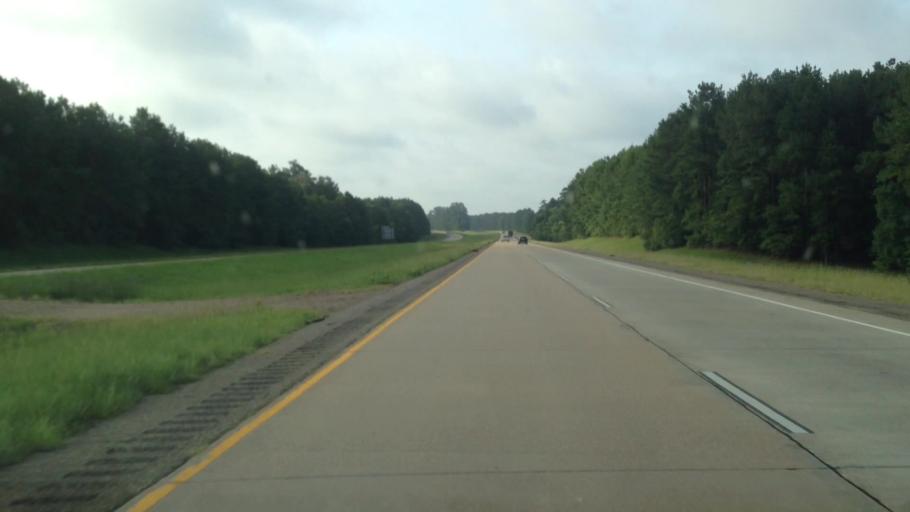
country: US
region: Louisiana
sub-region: Rapides Parish
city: Lecompte
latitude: 31.0448
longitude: -92.4186
